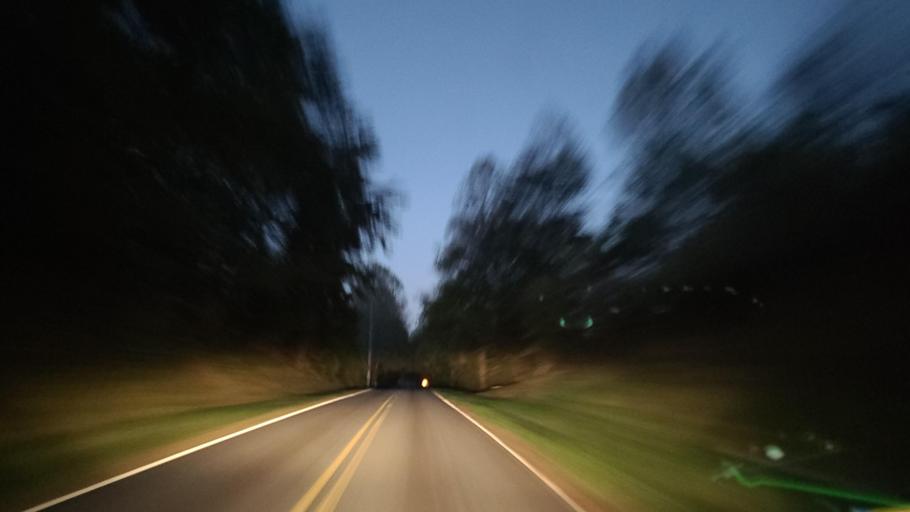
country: US
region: North Carolina
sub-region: Clay County
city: Hayesville
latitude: 34.9678
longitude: -83.8887
